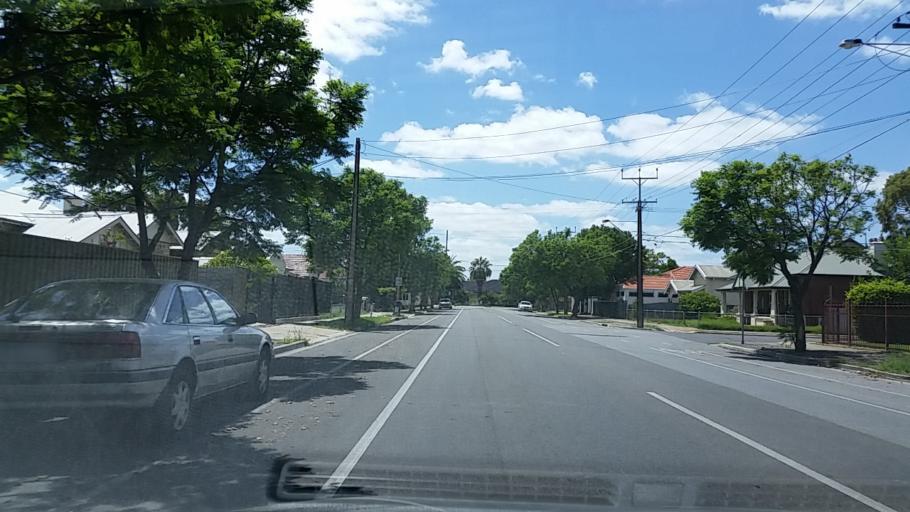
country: AU
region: South Australia
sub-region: City of West Torrens
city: Thebarton
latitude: -34.9293
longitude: 138.5593
